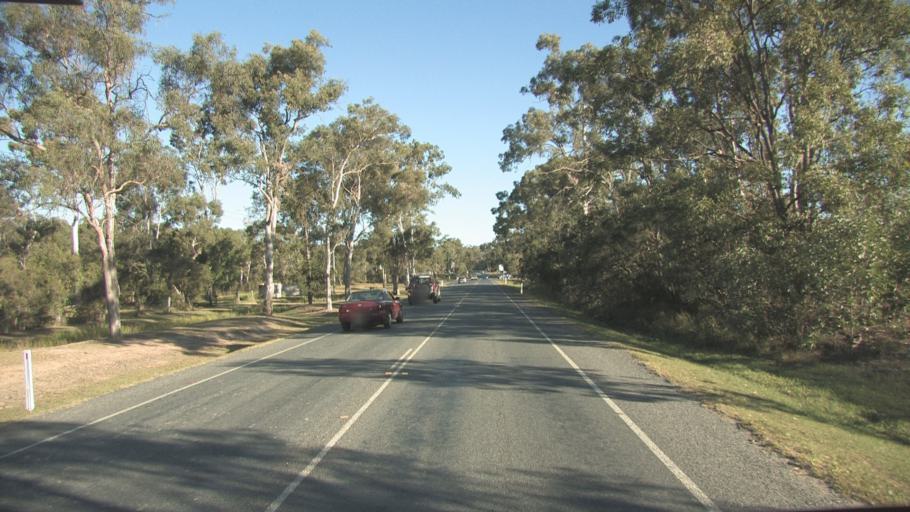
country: AU
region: Queensland
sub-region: Logan
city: Logan Reserve
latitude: -27.7191
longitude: 153.0914
